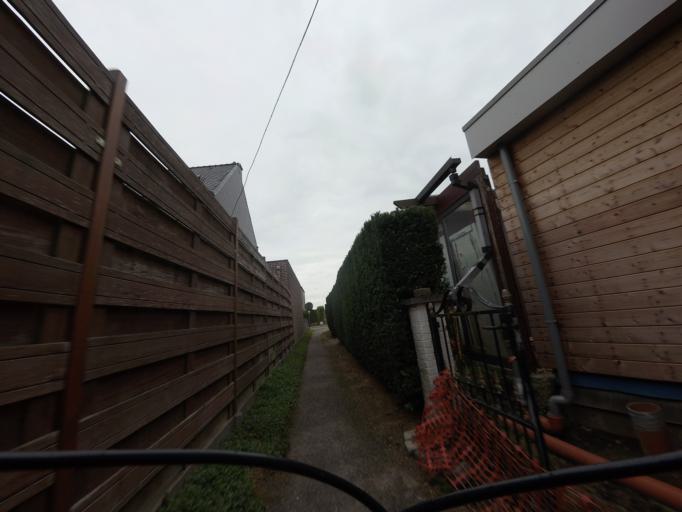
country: BE
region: Flanders
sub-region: Provincie Vlaams-Brabant
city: Grimbergen
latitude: 50.9378
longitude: 4.3873
